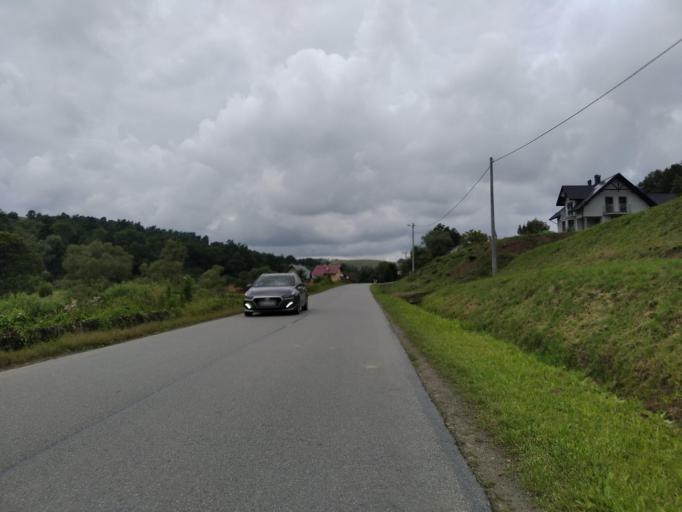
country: PL
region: Subcarpathian Voivodeship
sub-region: Powiat przemyski
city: Bircza
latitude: 49.6973
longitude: 22.3808
